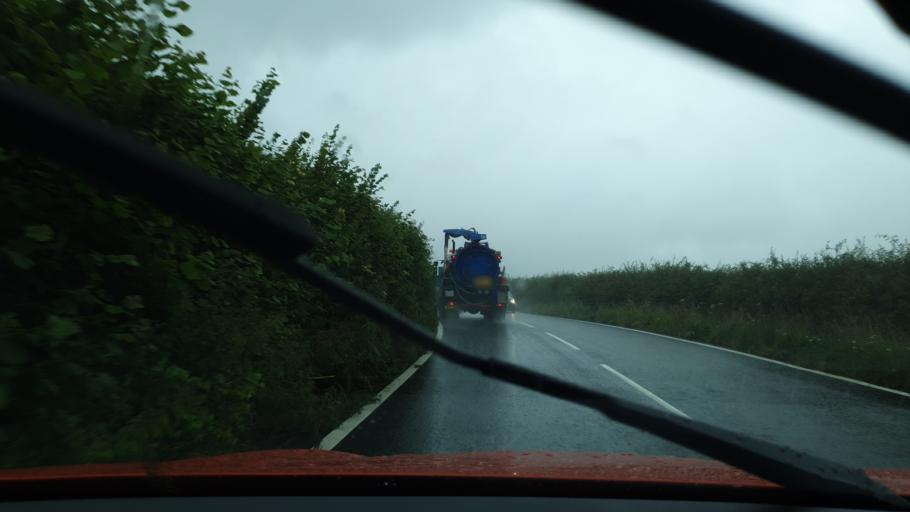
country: GB
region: England
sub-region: Cumbria
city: Millom
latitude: 54.2719
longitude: -3.2225
